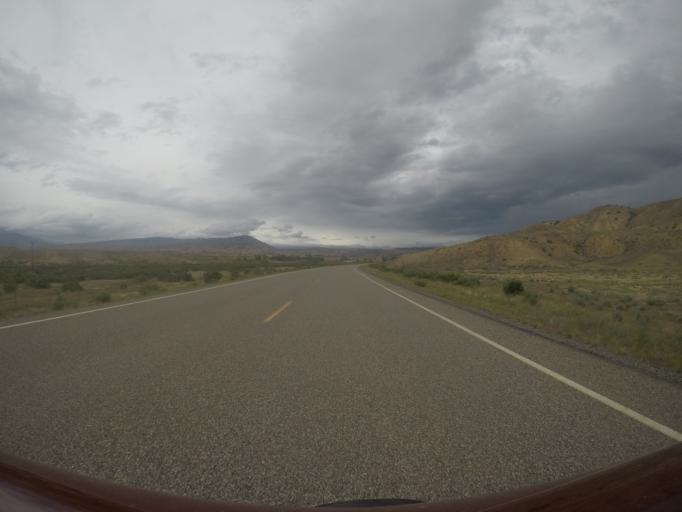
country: US
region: Wyoming
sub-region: Big Horn County
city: Lovell
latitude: 44.9531
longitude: -108.2948
